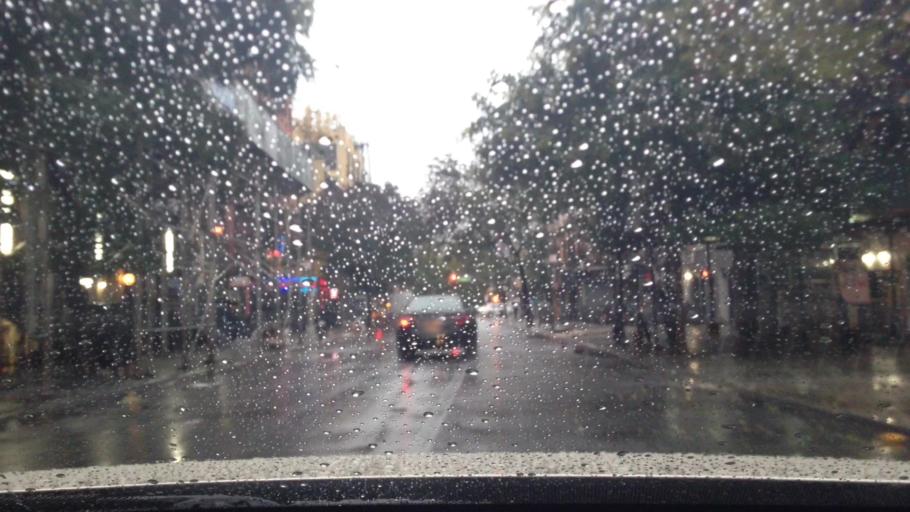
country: US
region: New York
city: New York City
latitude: 40.7294
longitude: -73.9890
